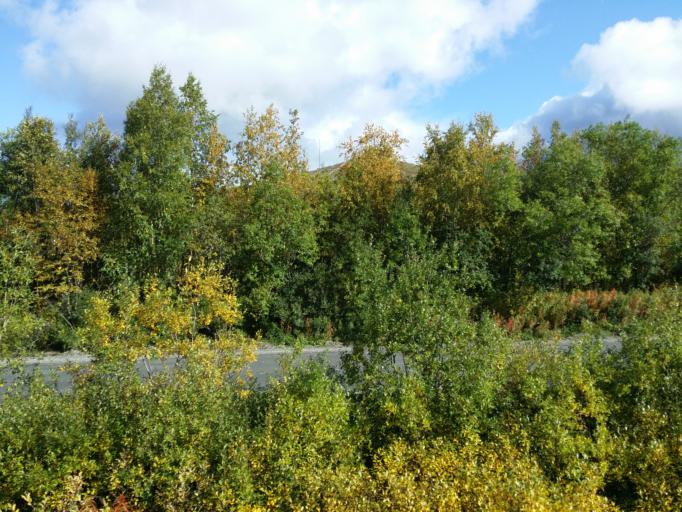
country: SE
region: Norrbotten
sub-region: Kiruna Kommun
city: Kiruna
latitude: 67.8717
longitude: 20.1951
